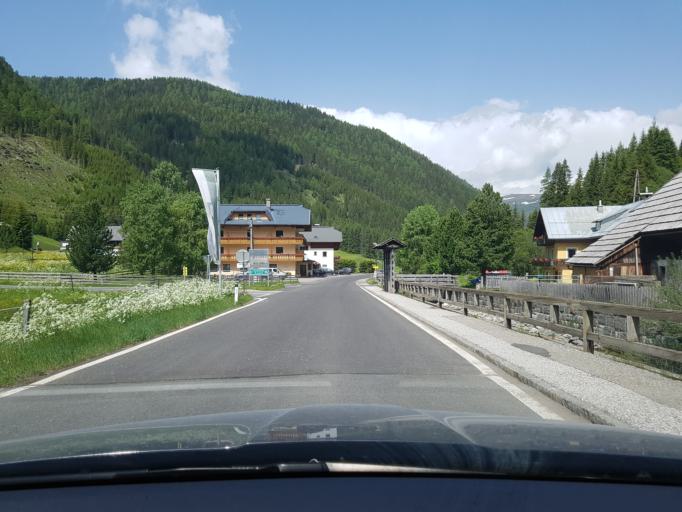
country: AT
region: Salzburg
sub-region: Politischer Bezirk Tamsweg
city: Thomatal
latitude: 46.9695
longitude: 13.7275
